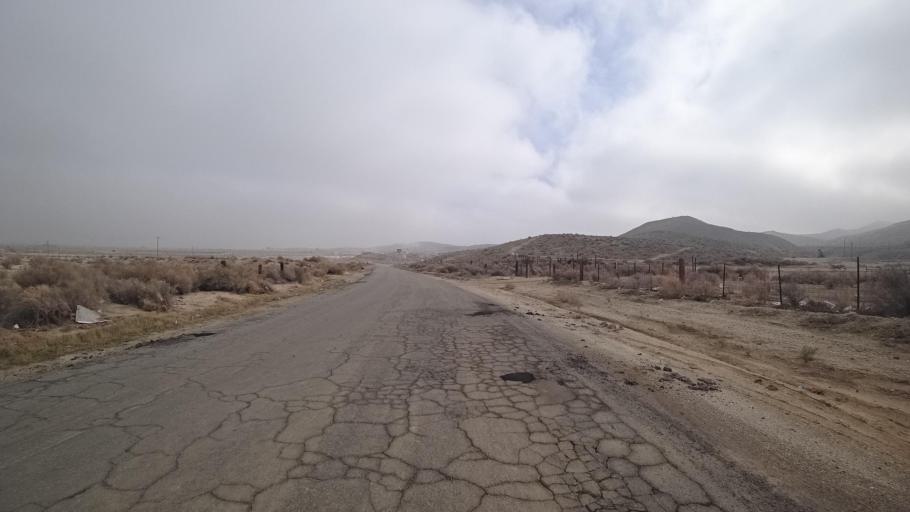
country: US
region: California
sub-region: Kern County
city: Maricopa
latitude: 35.0393
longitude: -119.3835
